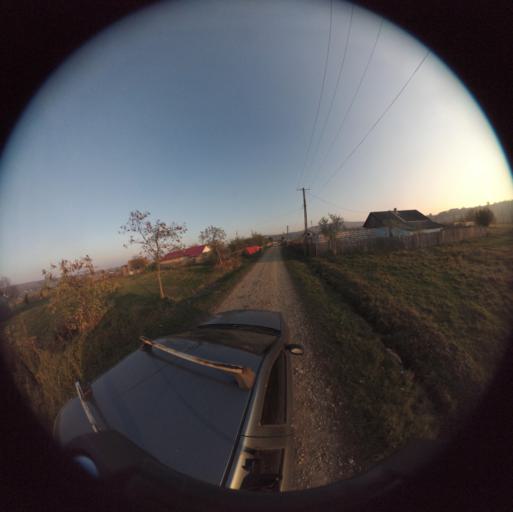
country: RO
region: Vaslui
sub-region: Comuna Bacesti
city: Bacesti
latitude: 46.8316
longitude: 27.2462
